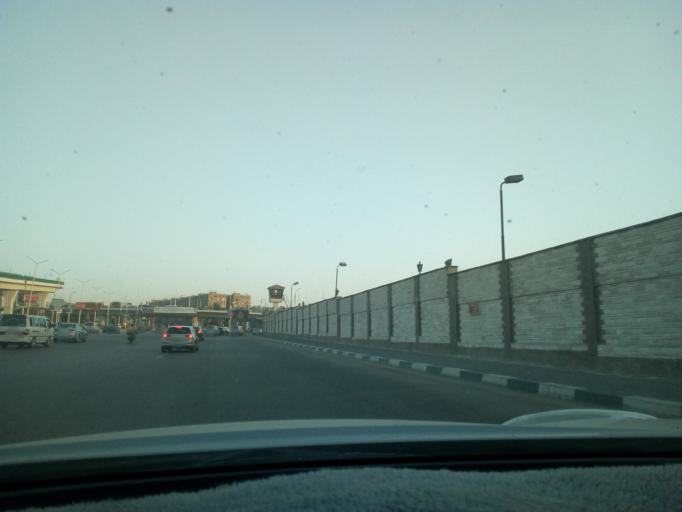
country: EG
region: Muhafazat al Qalyubiyah
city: Al Khankah
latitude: 30.1122
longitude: 31.3685
